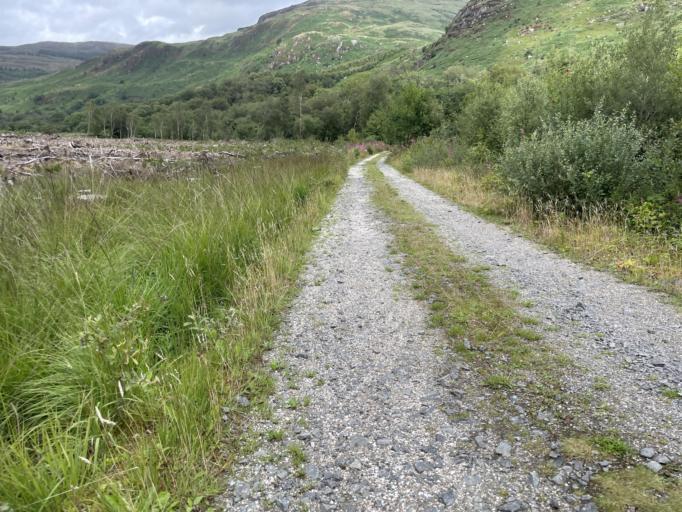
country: GB
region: Scotland
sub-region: Dumfries and Galloway
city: Newton Stewart
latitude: 55.0877
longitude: -4.4579
